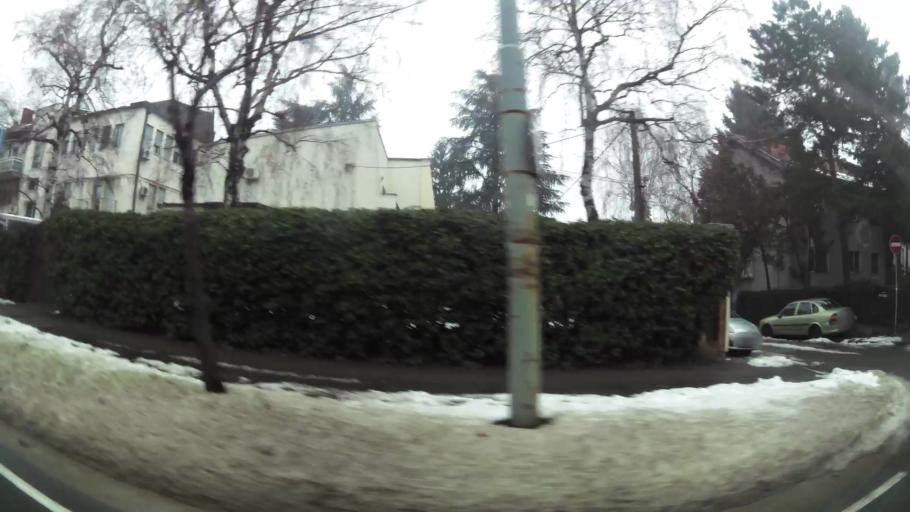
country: RS
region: Central Serbia
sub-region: Belgrade
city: Savski Venac
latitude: 44.7711
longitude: 20.4643
